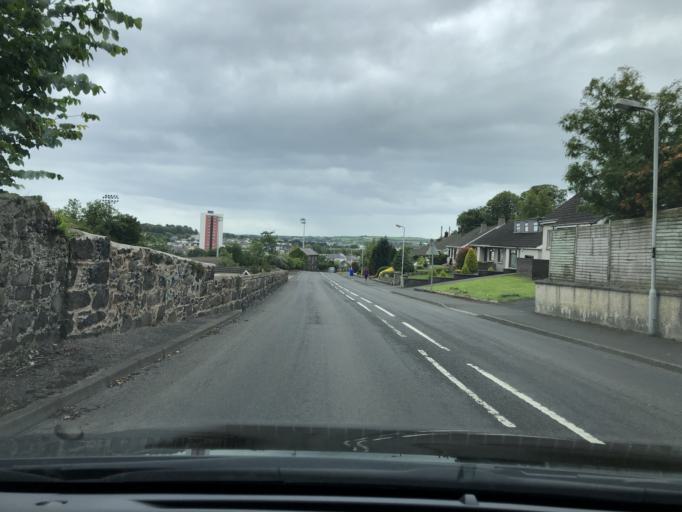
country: GB
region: Northern Ireland
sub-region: Larne District
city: Larne
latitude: 54.8492
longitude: -5.8311
